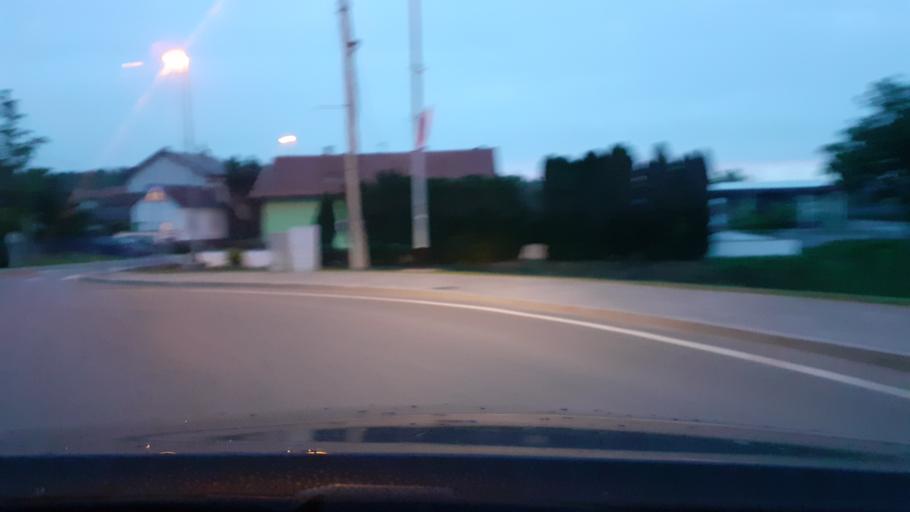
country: HR
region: Pozesko-Slavonska
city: Pleternica
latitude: 45.2838
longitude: 17.8045
